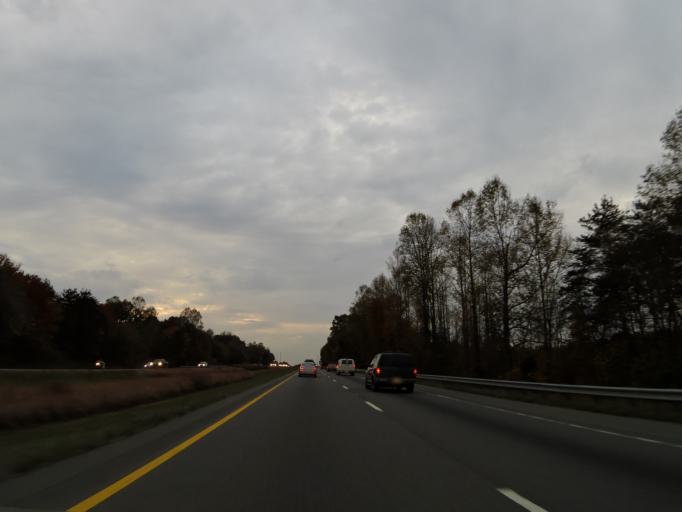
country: US
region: North Carolina
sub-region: Burke County
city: Hildebran
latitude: 35.7057
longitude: -81.4116
